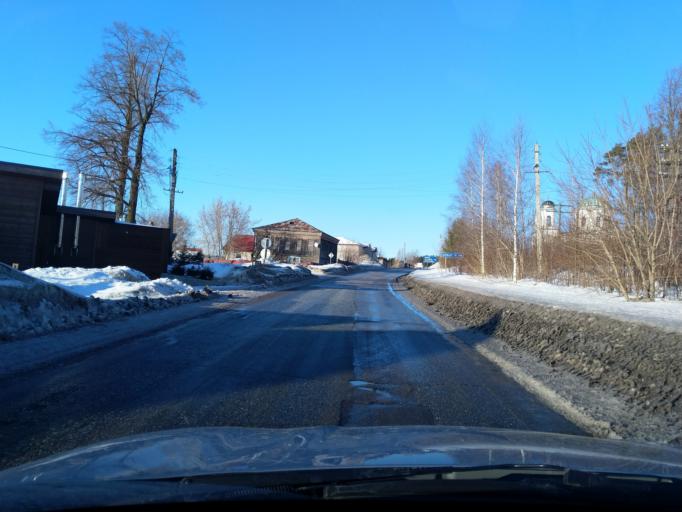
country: RU
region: Perm
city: Polazna
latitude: 58.3062
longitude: 56.4195
